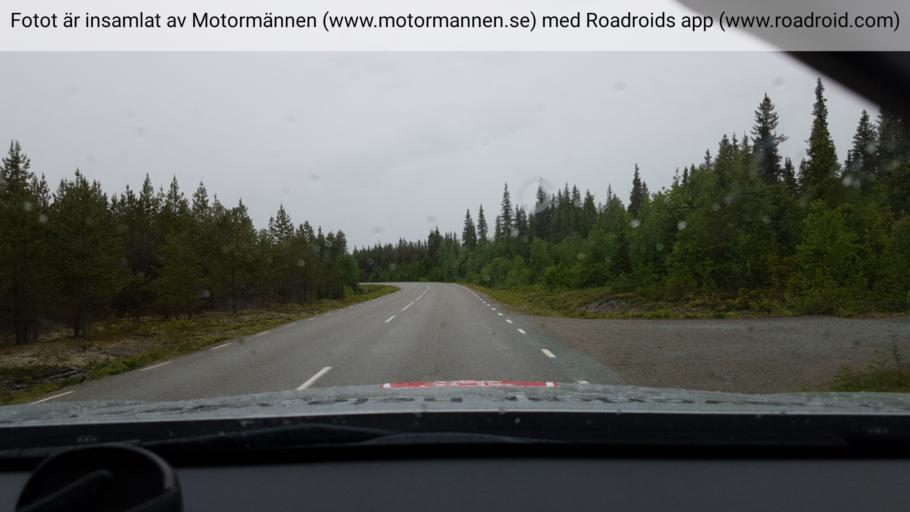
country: SE
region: Vaesterbotten
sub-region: Storumans Kommun
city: Fristad
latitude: 65.8535
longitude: 16.5047
